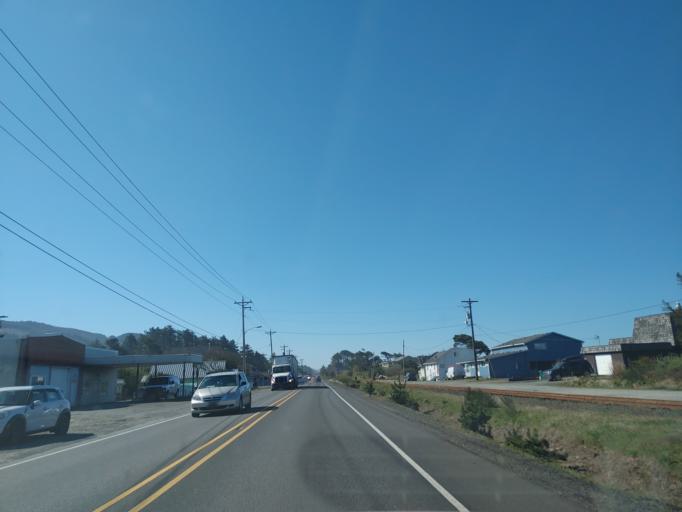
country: US
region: Oregon
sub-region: Tillamook County
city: Rockaway Beach
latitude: 45.6066
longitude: -123.9450
